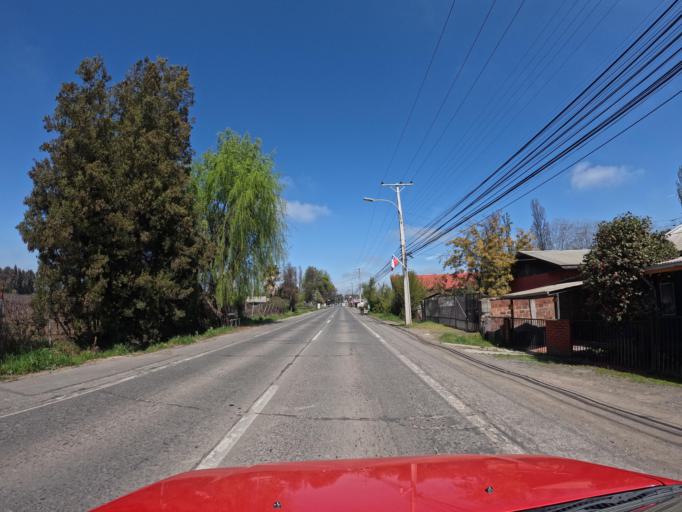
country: CL
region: Maule
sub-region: Provincia de Curico
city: Molina
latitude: -35.0811
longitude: -71.2625
